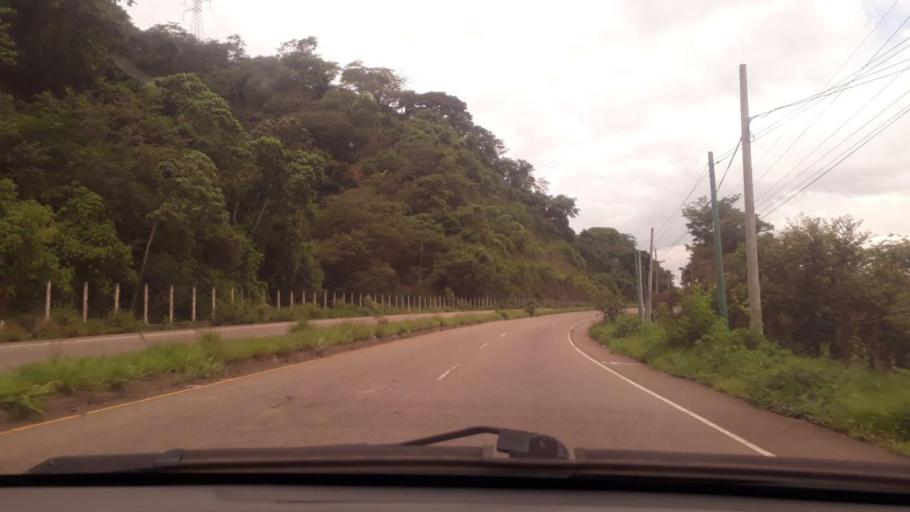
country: GT
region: Santa Rosa
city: Oratorio
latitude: 14.2563
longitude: -90.2172
